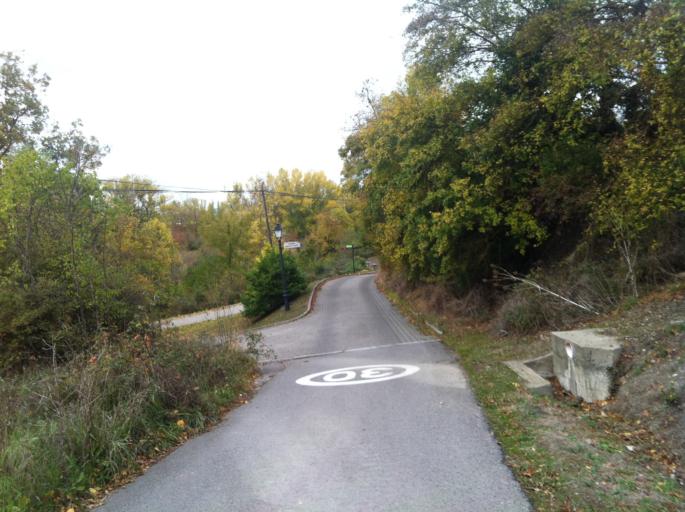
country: ES
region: Basque Country
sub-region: Provincia de Alava
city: Gasteiz / Vitoria
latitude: 42.8307
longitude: -2.7000
